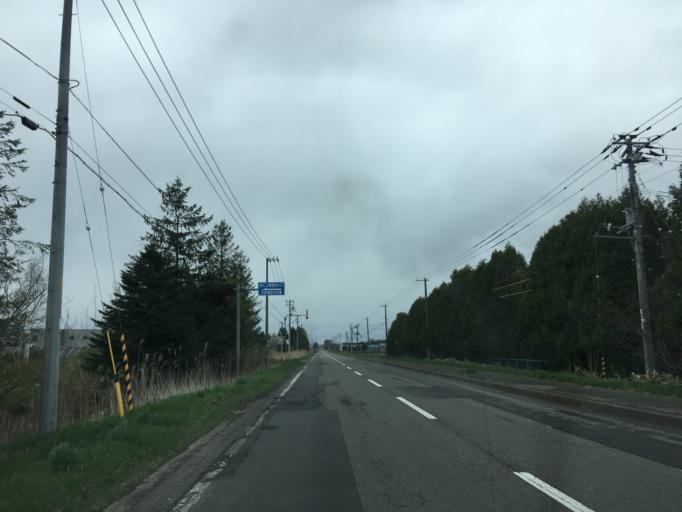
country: JP
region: Hokkaido
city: Chitose
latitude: 42.9314
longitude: 141.8067
